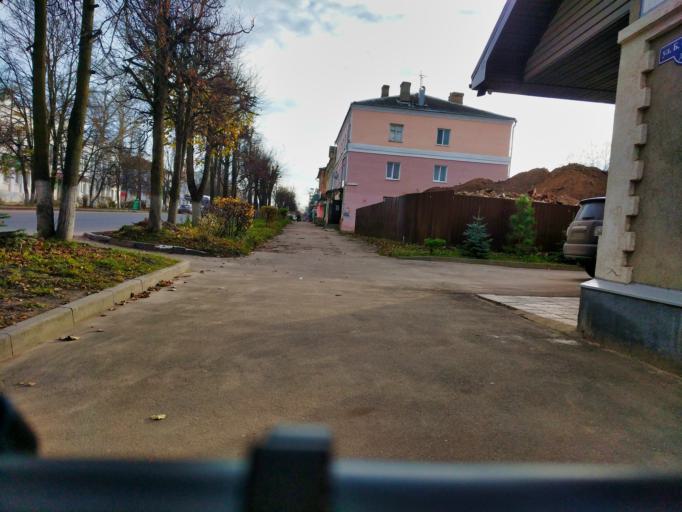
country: RU
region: Tverskaya
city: Rzhev
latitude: 56.2548
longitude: 34.3277
